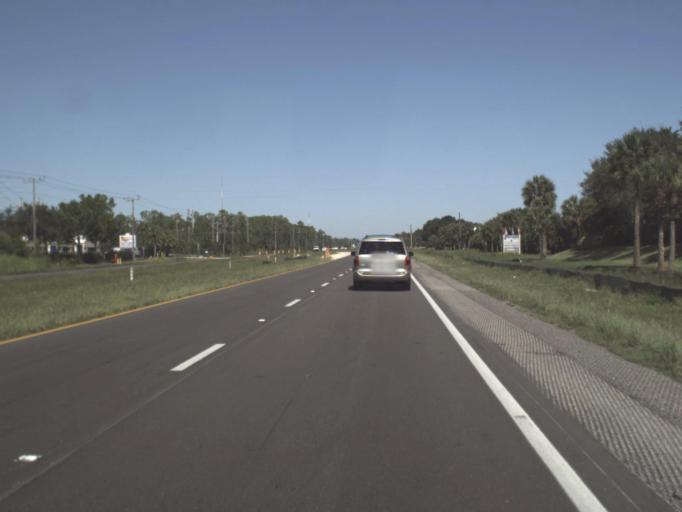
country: US
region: Florida
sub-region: Collier County
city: Lely Resort
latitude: 26.0343
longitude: -81.7004
